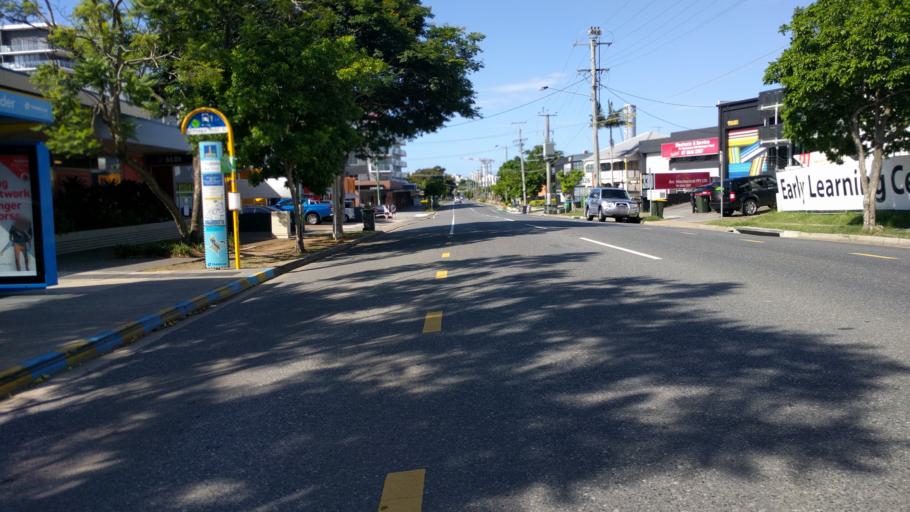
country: AU
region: Queensland
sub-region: Brisbane
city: Milton
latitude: -27.4825
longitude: 153.0038
